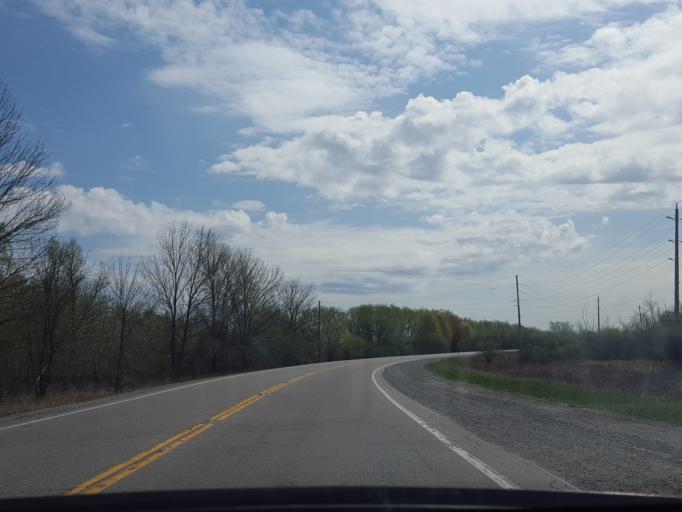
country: CA
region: Ontario
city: Oshawa
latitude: 44.1072
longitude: -78.9023
